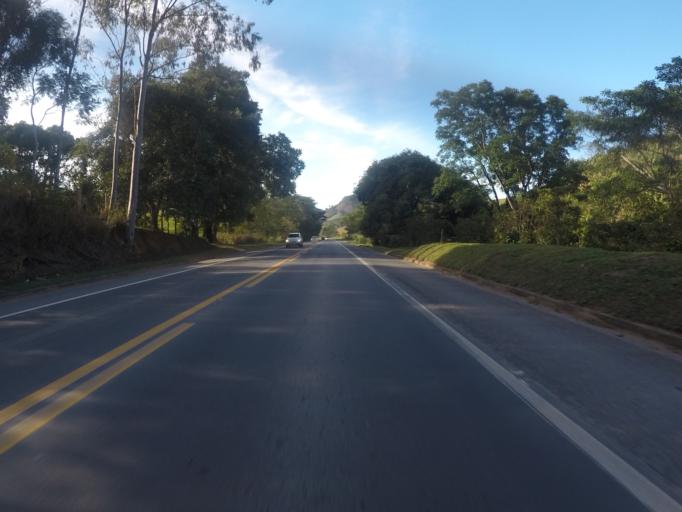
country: BR
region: Espirito Santo
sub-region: Fundao
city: Fundao
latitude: -19.8764
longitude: -40.4149
